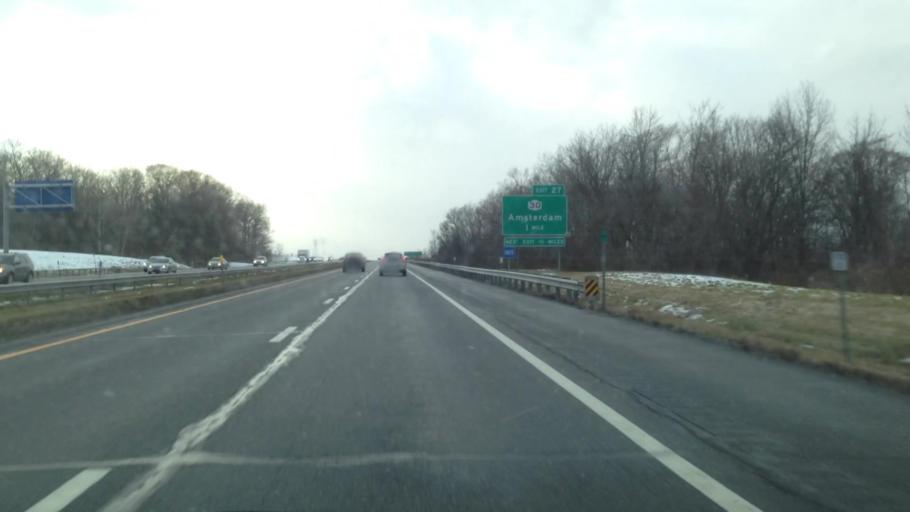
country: US
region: New York
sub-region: Montgomery County
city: Amsterdam
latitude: 42.9174
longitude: -74.1701
